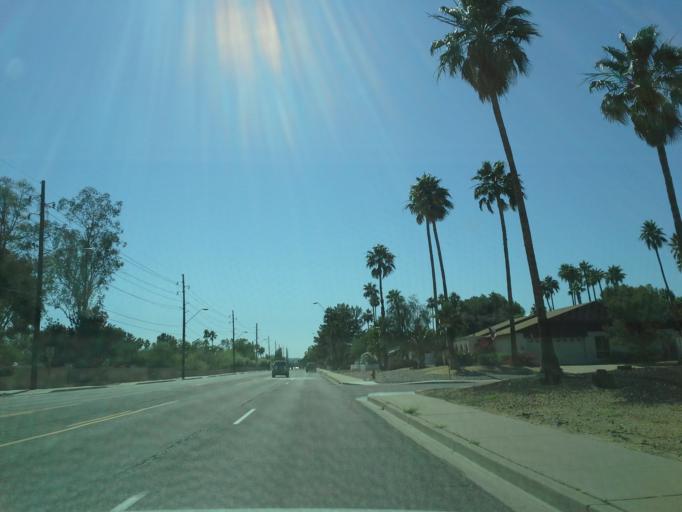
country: US
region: Arizona
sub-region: Maricopa County
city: Paradise Valley
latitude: 33.5971
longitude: -111.9542
